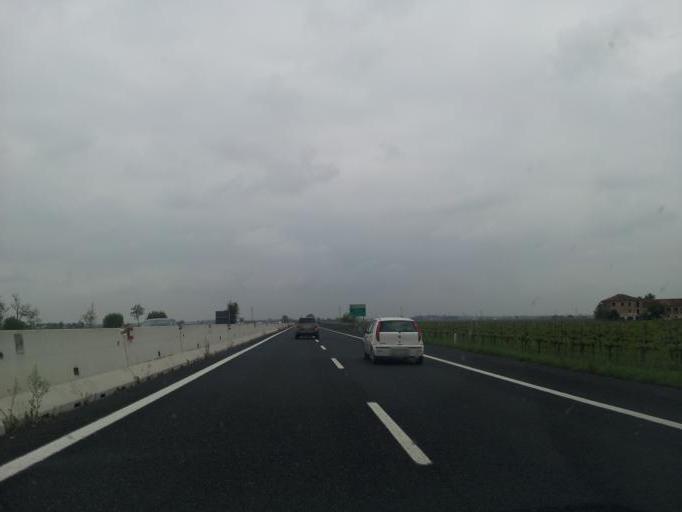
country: IT
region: Veneto
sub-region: Provincia di Treviso
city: Cessalto
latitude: 45.7139
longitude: 12.6249
